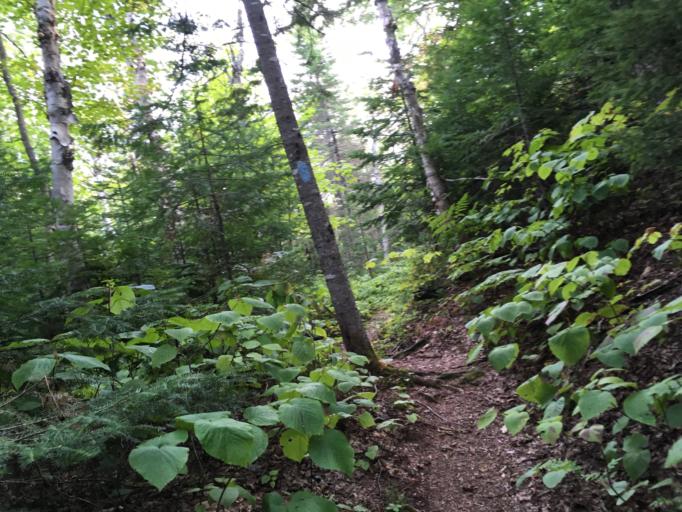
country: US
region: Maine
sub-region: Penobscot County
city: Millinocket
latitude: 45.9190
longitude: -68.8528
